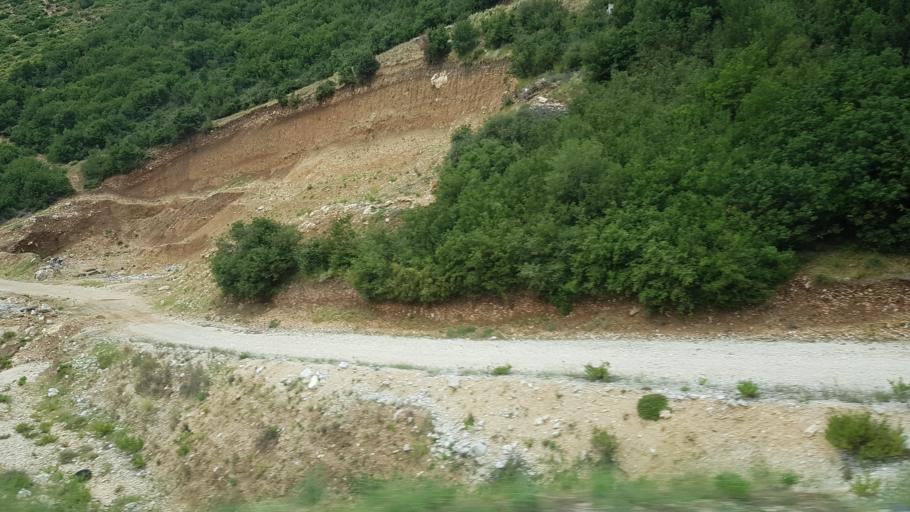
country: AL
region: Fier
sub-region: Rrethi i Mallakastres
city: Kute
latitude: 40.5107
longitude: 19.7522
